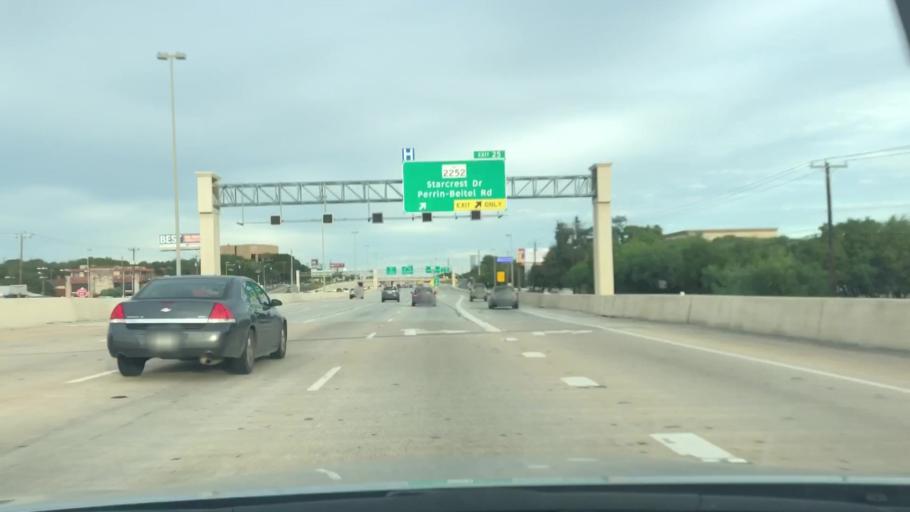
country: US
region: Texas
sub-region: Bexar County
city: Terrell Hills
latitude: 29.5159
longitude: -98.4296
